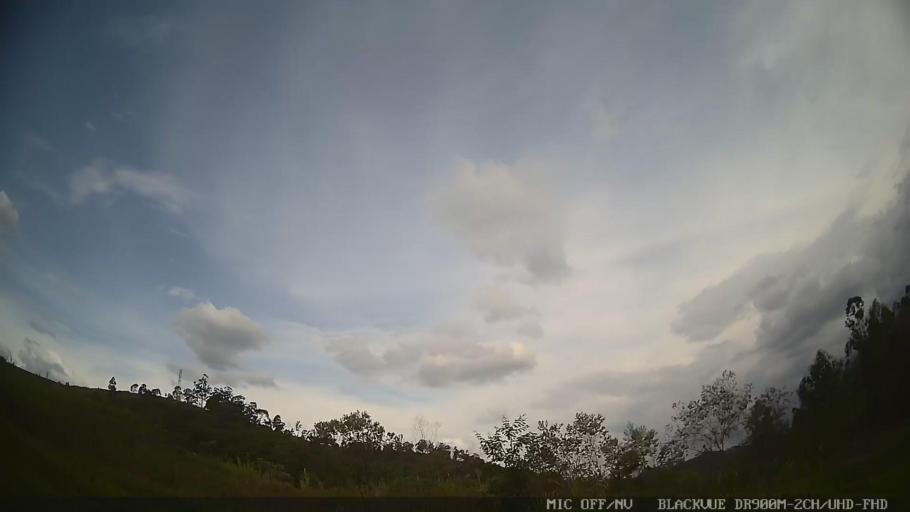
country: BR
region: Sao Paulo
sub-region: Amparo
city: Amparo
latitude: -22.7600
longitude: -46.7562
